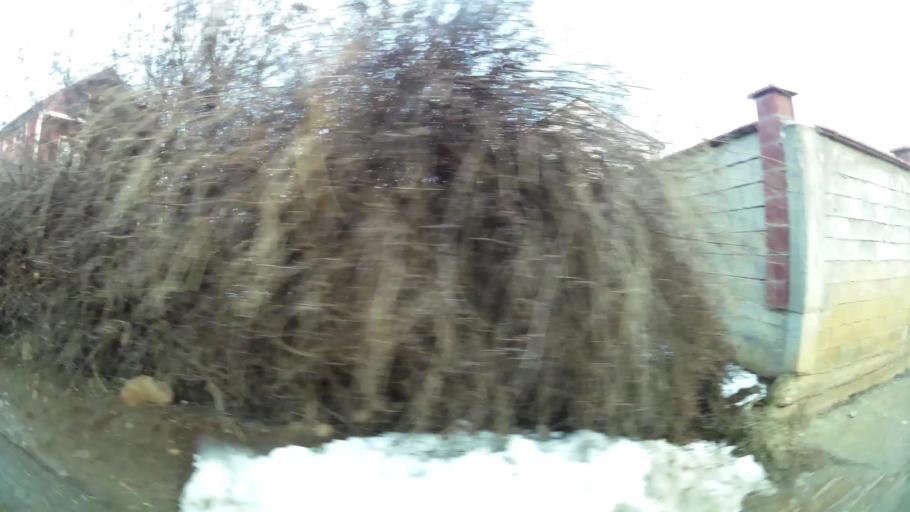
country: MK
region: Aracinovo
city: Arachinovo
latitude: 42.0283
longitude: 21.5753
